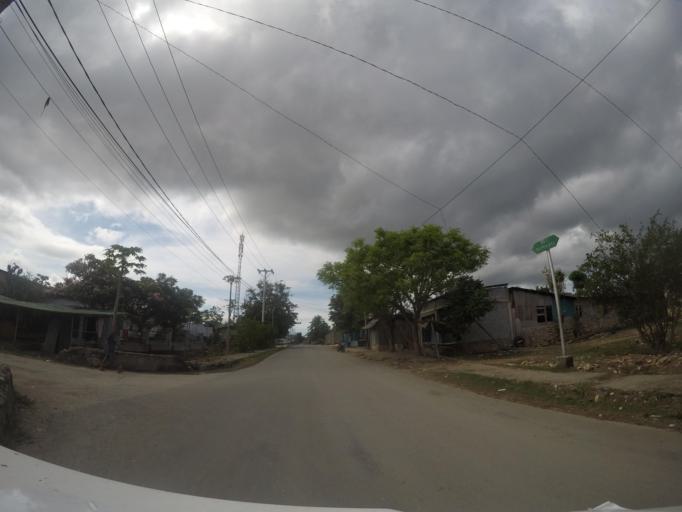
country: TL
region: Baucau
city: Baucau
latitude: -8.4734
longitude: 126.4561
